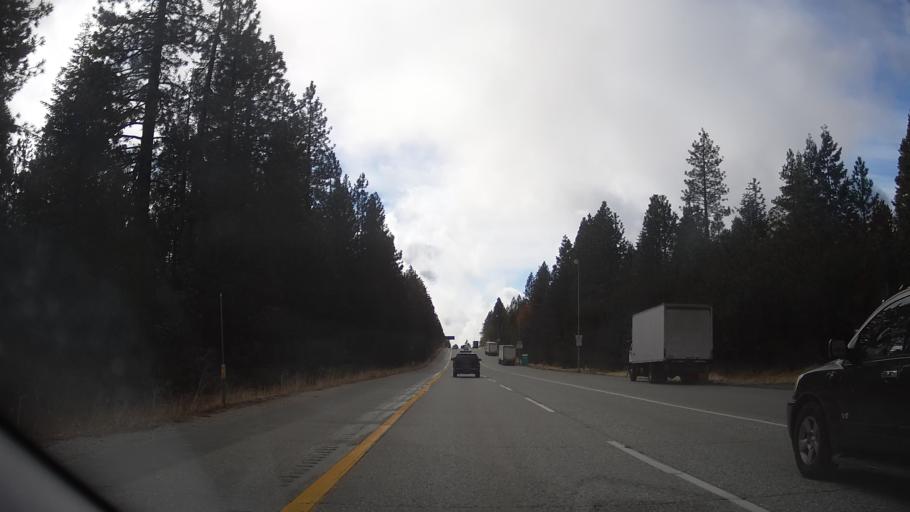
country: US
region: California
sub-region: Placer County
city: Foresthill
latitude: 39.2895
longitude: -120.6926
